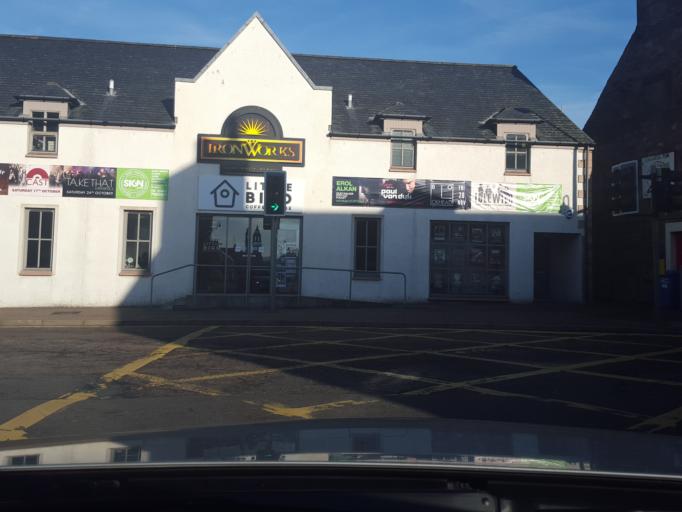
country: GB
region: Scotland
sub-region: Highland
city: Inverness
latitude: 57.4807
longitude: -4.2284
